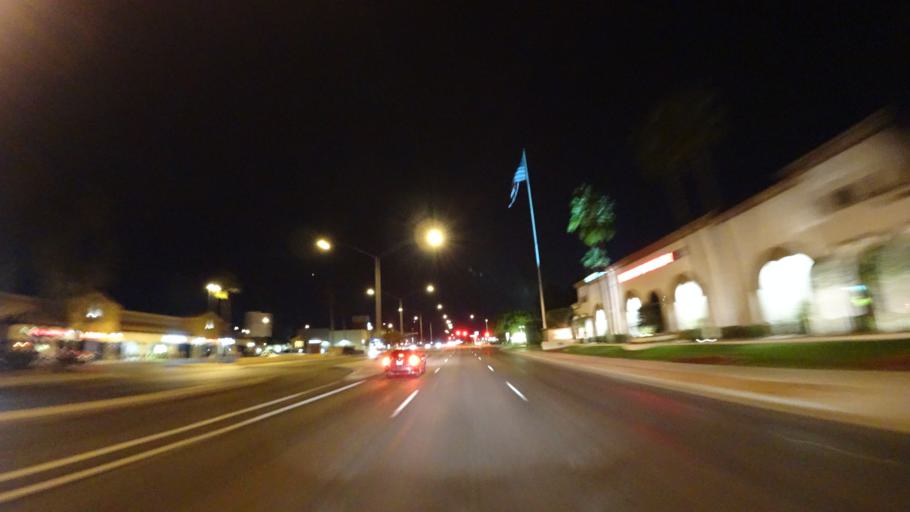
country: US
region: Arizona
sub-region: Maricopa County
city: San Carlos
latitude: 33.3788
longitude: -111.8579
